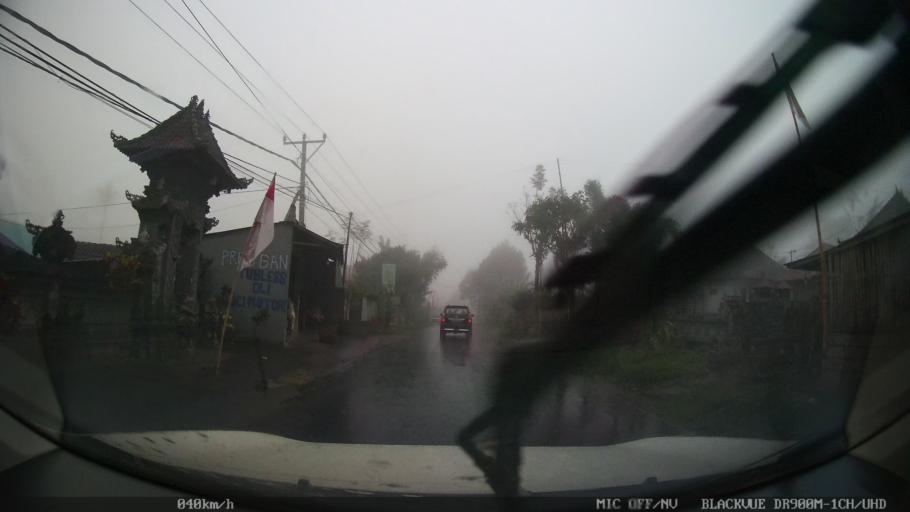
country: ID
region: Bali
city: Banjar Taro Kelod
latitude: -8.3191
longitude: 115.2981
